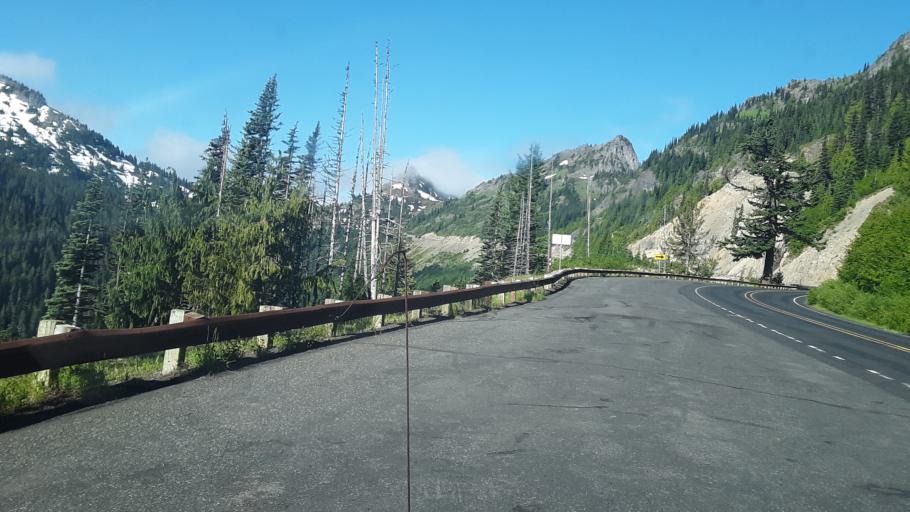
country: US
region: Washington
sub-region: King County
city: Enumclaw
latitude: 46.8887
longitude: -121.4970
